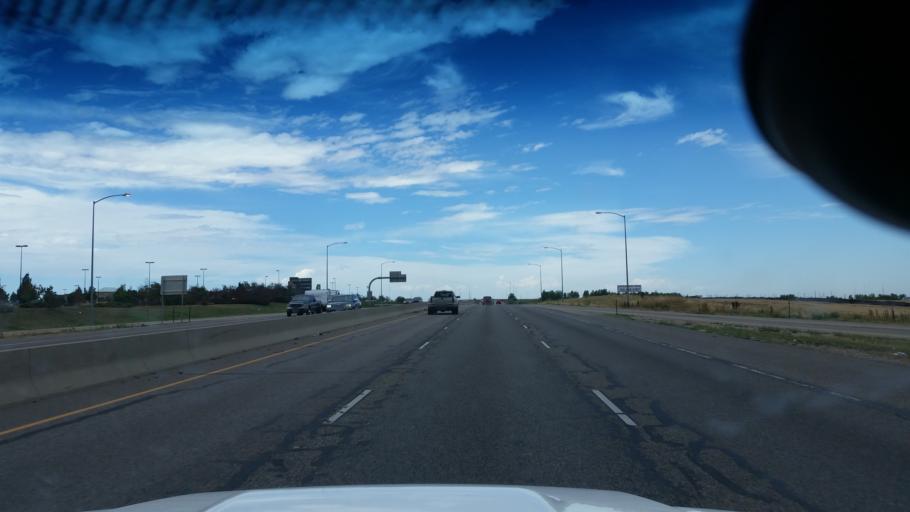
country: US
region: Colorado
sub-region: Adams County
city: Northglenn
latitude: 39.9609
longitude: -104.9879
